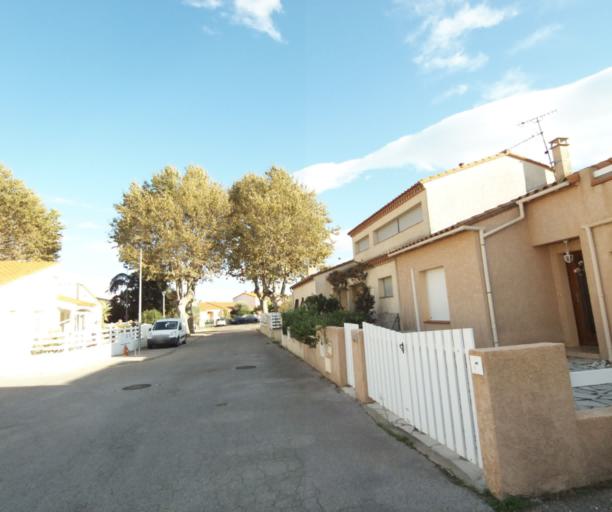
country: FR
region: Languedoc-Roussillon
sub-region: Departement des Pyrenees-Orientales
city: Argelers
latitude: 42.5488
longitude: 3.0294
